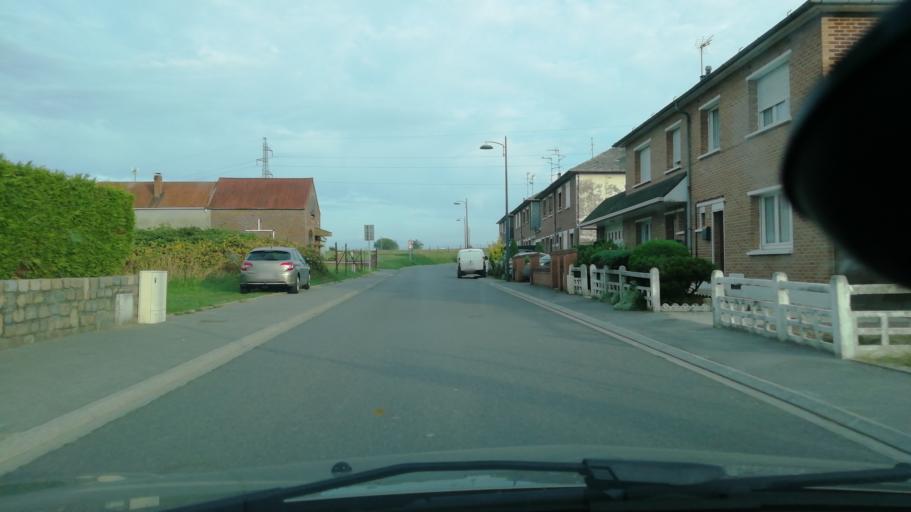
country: FR
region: Nord-Pas-de-Calais
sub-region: Departement du Nord
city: Viesly
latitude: 50.1189
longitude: 3.4664
